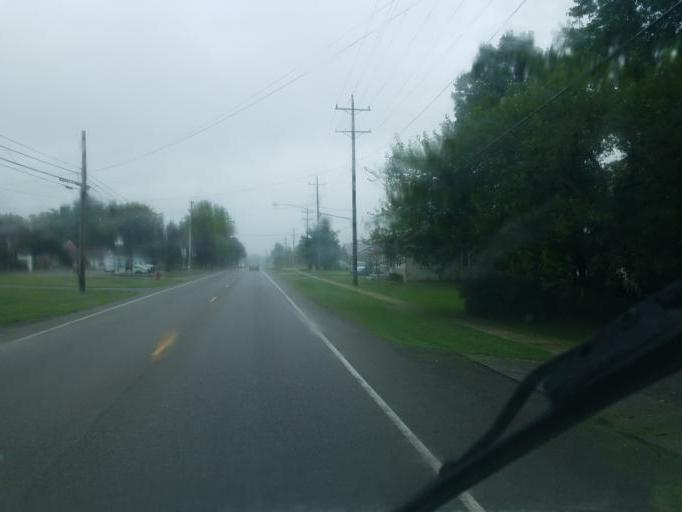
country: US
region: Ohio
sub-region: Licking County
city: Johnstown
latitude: 40.1579
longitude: -82.6888
